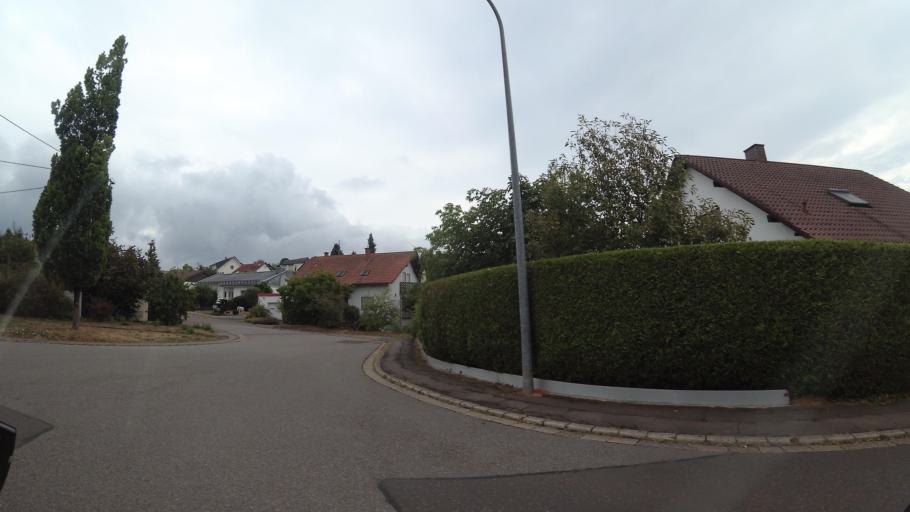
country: DE
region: Saarland
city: Sankt Ingbert
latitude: 49.2220
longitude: 7.1596
